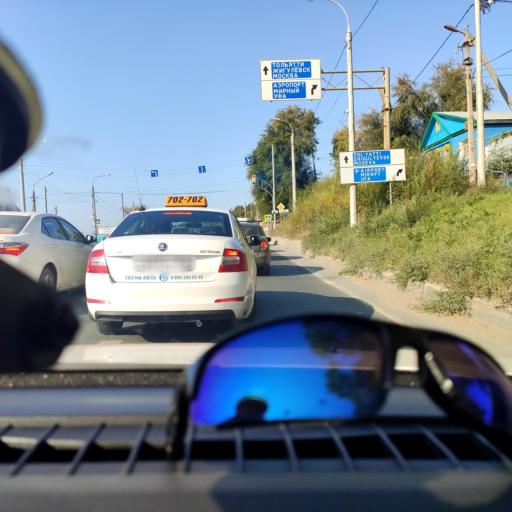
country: RU
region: Samara
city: Volzhskiy
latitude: 53.4305
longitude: 50.1187
